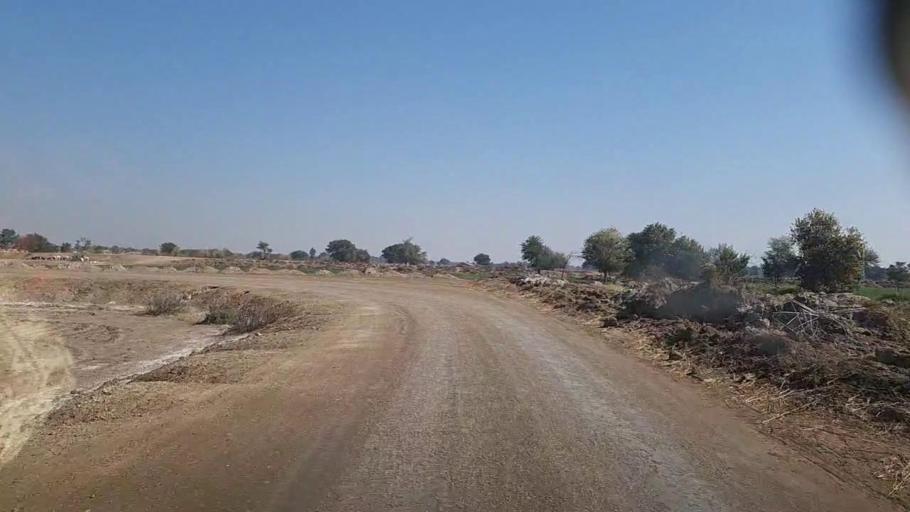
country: PK
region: Sindh
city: Khairpur
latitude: 27.9794
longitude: 69.8491
